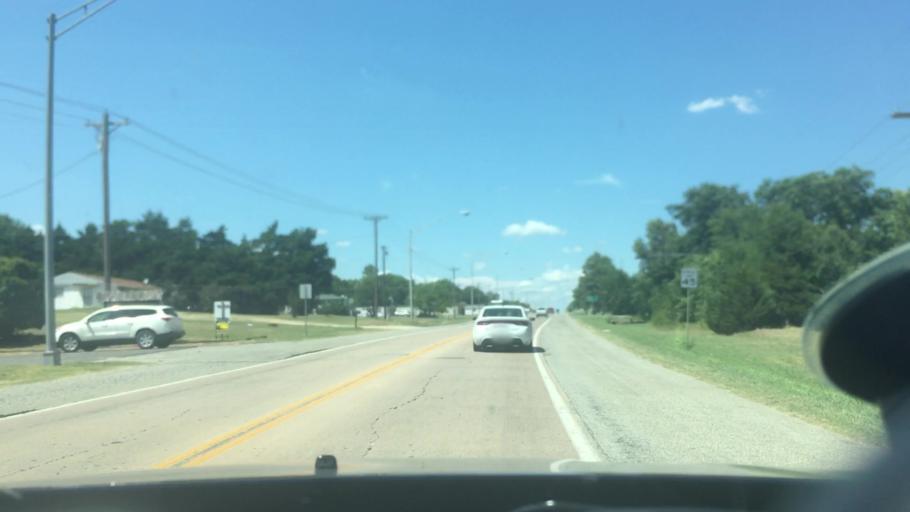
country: US
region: Oklahoma
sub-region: Marshall County
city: Kingston
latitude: 34.0026
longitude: -96.7262
